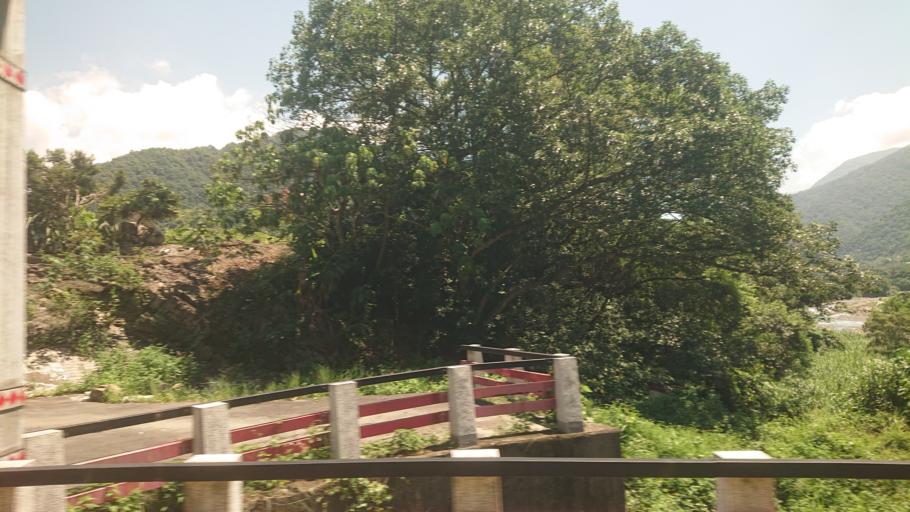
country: TW
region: Taiwan
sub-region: Nantou
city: Puli
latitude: 24.0637
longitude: 120.9539
